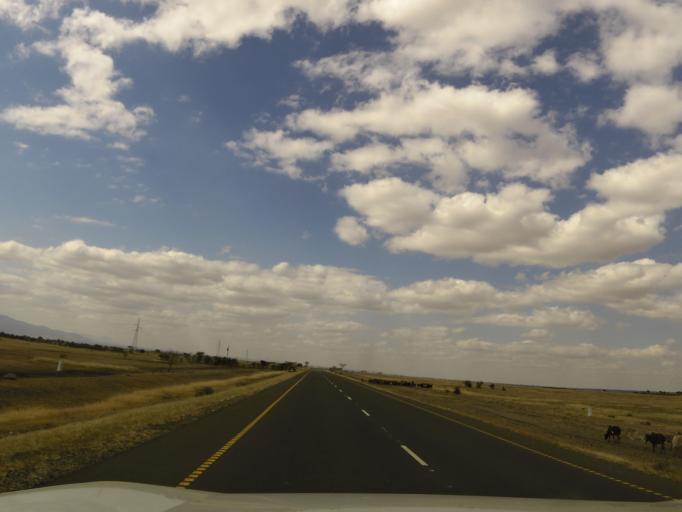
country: TZ
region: Arusha
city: Mto wa Mbu
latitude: -3.6164
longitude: 36.0342
